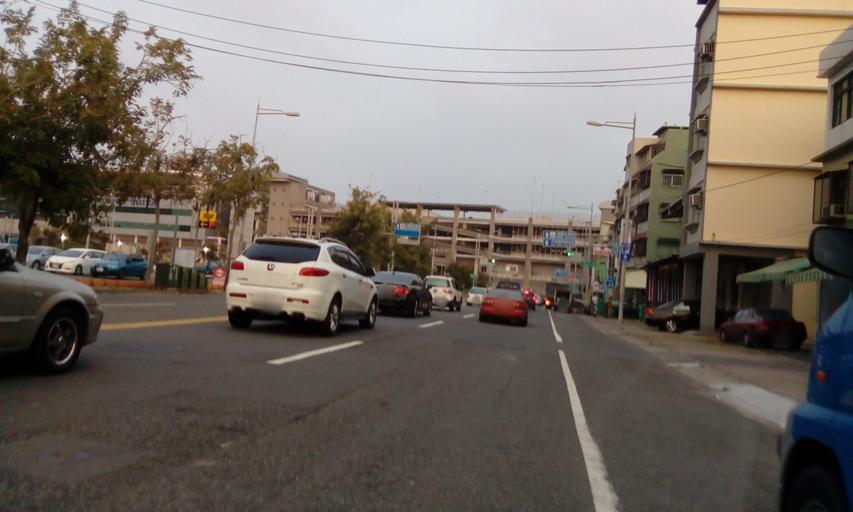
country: TW
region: Kaohsiung
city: Kaohsiung
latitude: 22.6876
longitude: 120.3040
